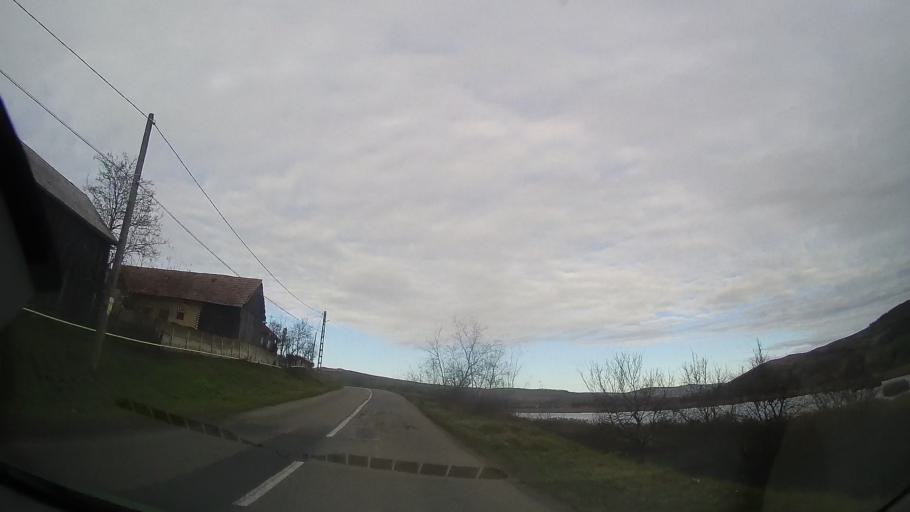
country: RO
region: Cluj
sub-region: Comuna Geaca
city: Geaca
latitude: 46.8367
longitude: 24.1304
